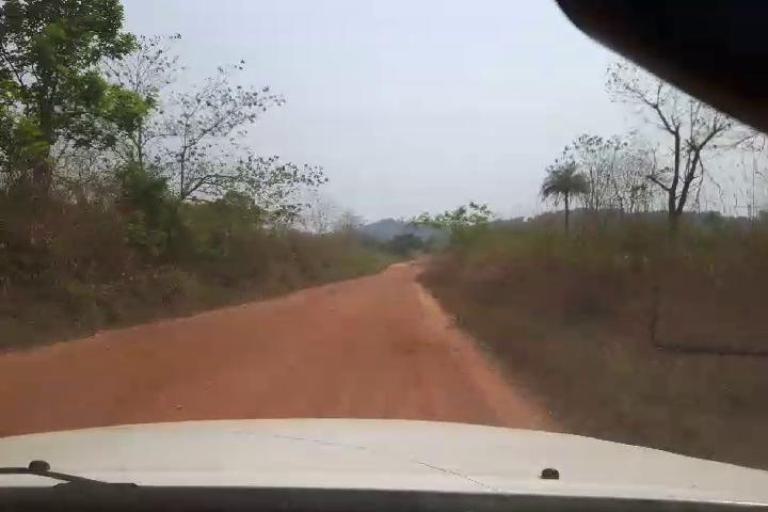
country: SL
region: Northern Province
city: Bumbuna
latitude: 8.9436
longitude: -11.8145
